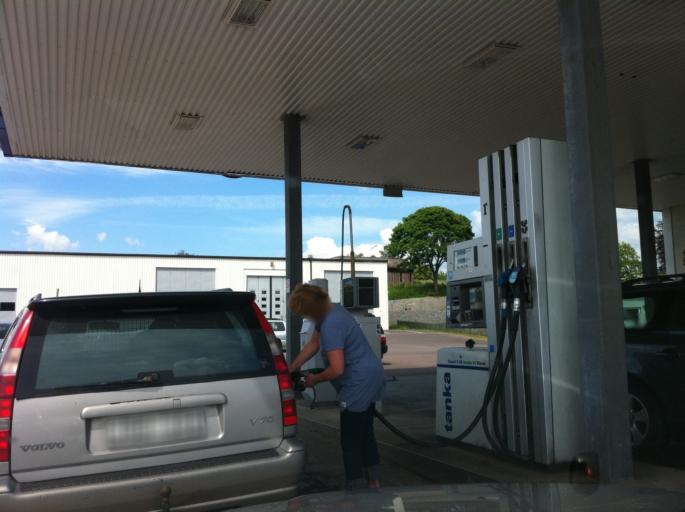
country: SE
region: Vaermland
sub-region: Sunne Kommun
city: Sunne
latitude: 59.8380
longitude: 13.1284
